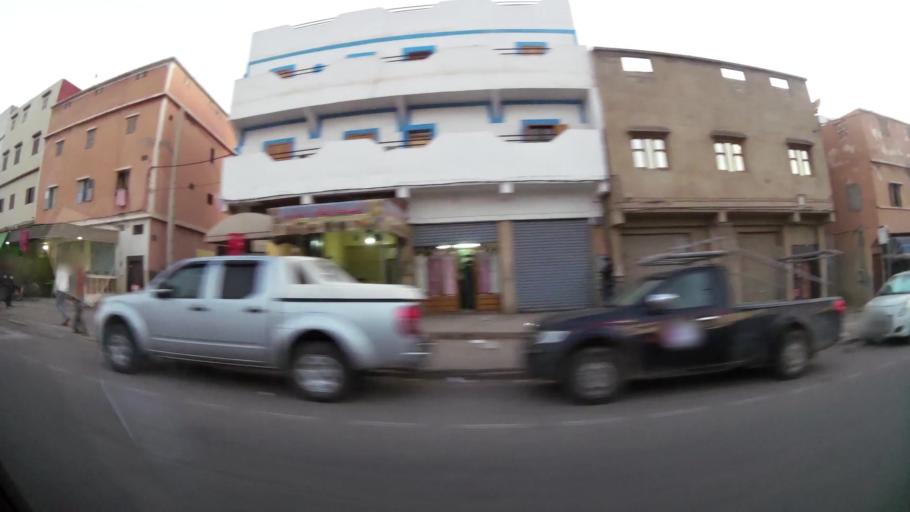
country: MA
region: Souss-Massa-Draa
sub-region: Inezgane-Ait Mellou
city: Inezgane
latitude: 30.3771
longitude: -9.4973
